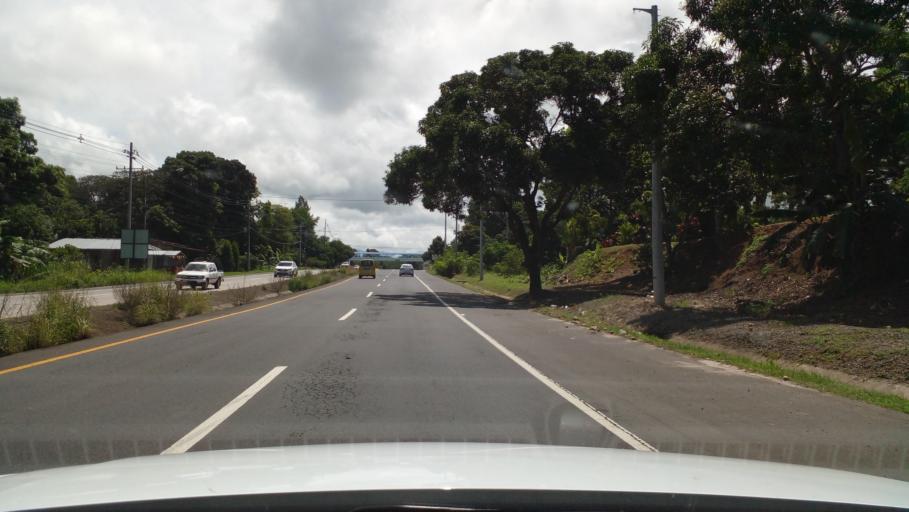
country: PA
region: Cocle
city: Rio Hato
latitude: 8.4214
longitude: -80.0745
